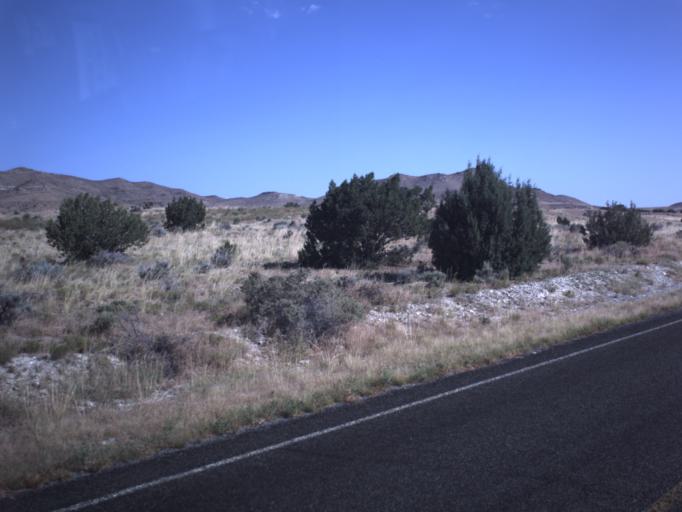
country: US
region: Utah
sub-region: Beaver County
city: Milford
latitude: 38.8385
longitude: -112.8463
